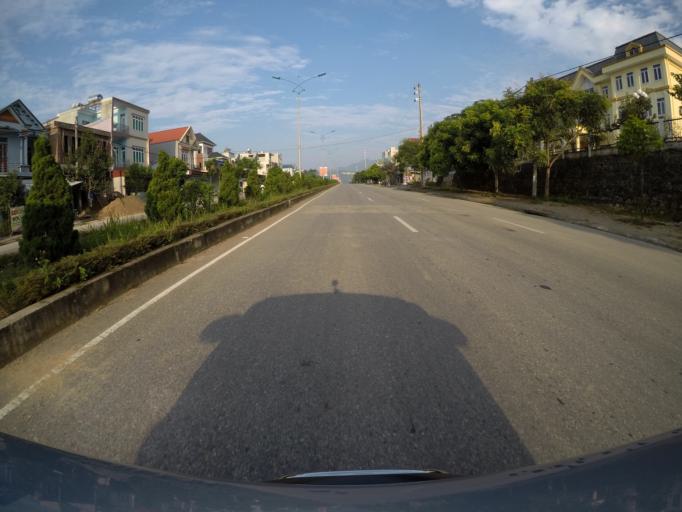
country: VN
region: Lai Chau
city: Tam Duong
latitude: 22.3225
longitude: 103.6219
